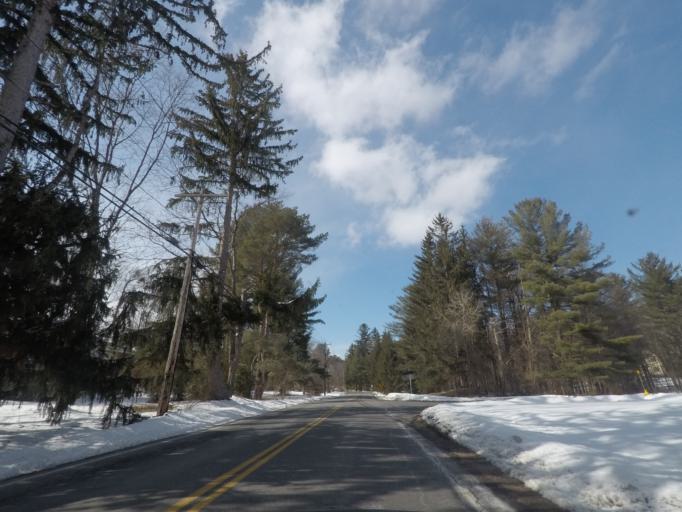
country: US
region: New York
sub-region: Albany County
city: Delmar
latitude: 42.6317
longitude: -73.8721
